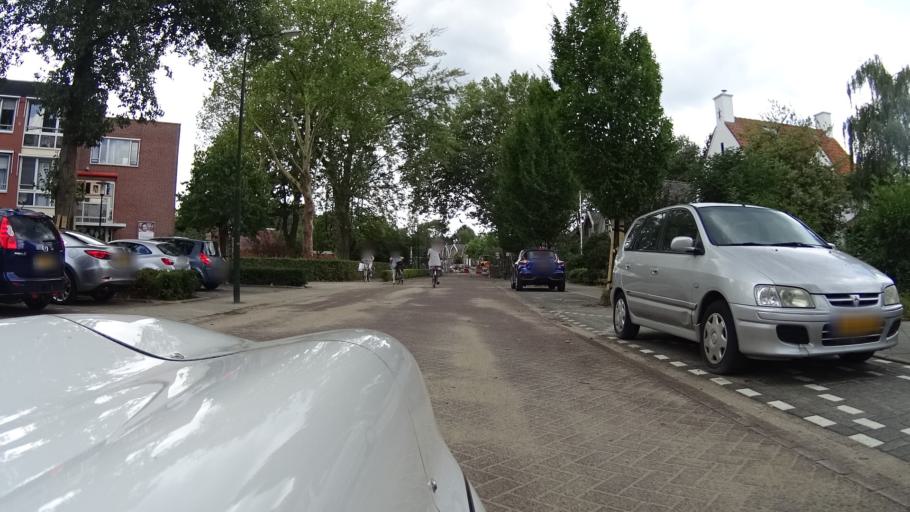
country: NL
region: South Holland
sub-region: Gemeente Hardinxveld-Giessendam
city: Boven-Hardinxveld
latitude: 51.8242
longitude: 4.8833
